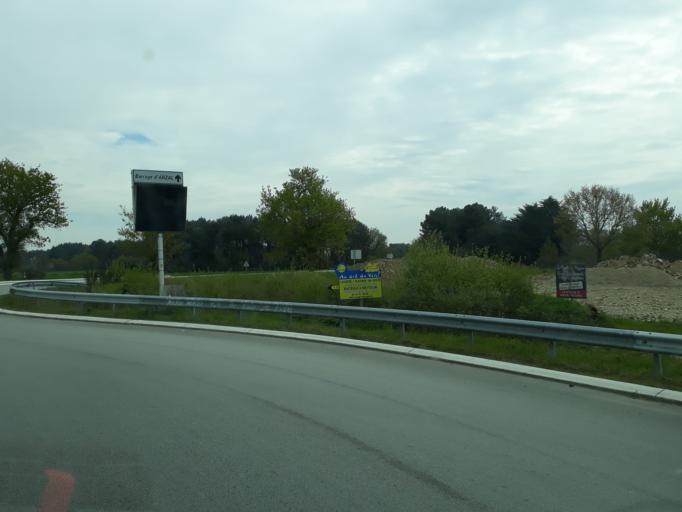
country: FR
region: Brittany
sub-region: Departement du Morbihan
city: Peaule
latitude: 47.5349
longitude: -2.3962
